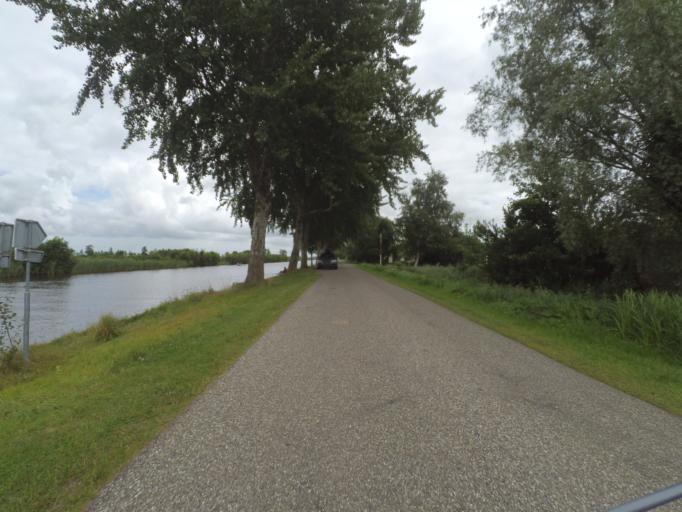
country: NL
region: Friesland
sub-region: Gemeente Kollumerland en Nieuwkruisland
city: Kollumerzwaag
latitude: 53.2948
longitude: 6.0906
